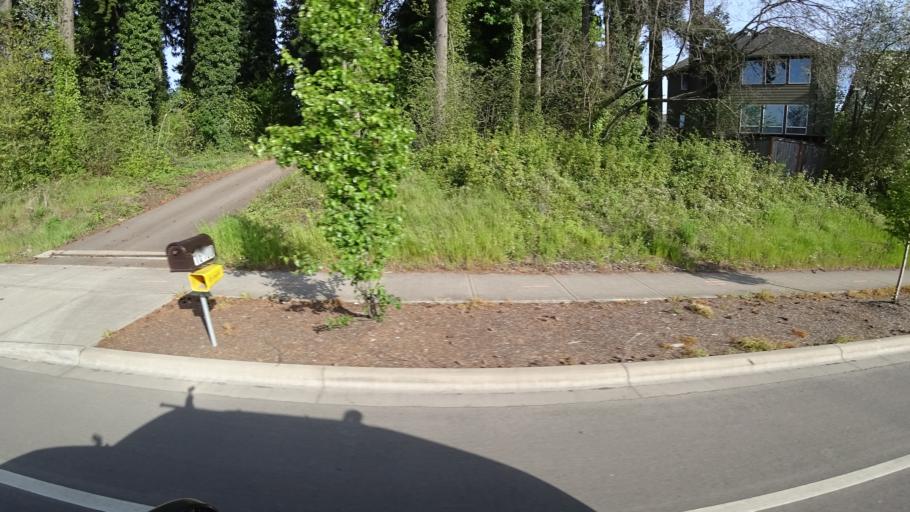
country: US
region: Oregon
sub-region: Washington County
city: King City
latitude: 45.4302
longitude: -122.8427
